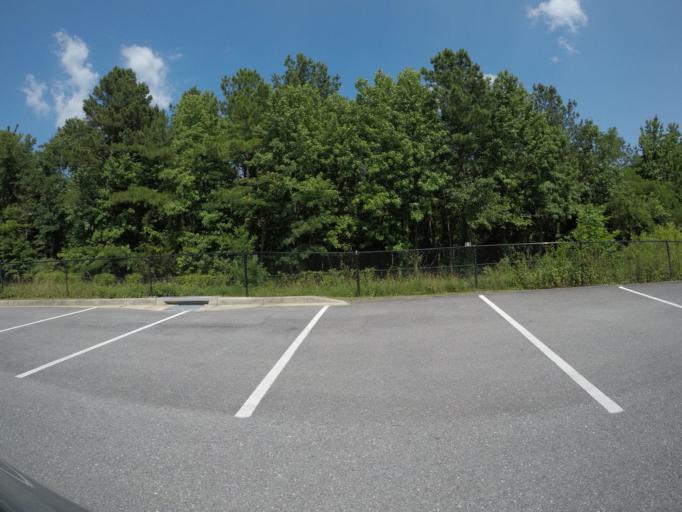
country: US
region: Maryland
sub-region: Harford County
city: Edgewood
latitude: 39.4338
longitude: -76.3093
